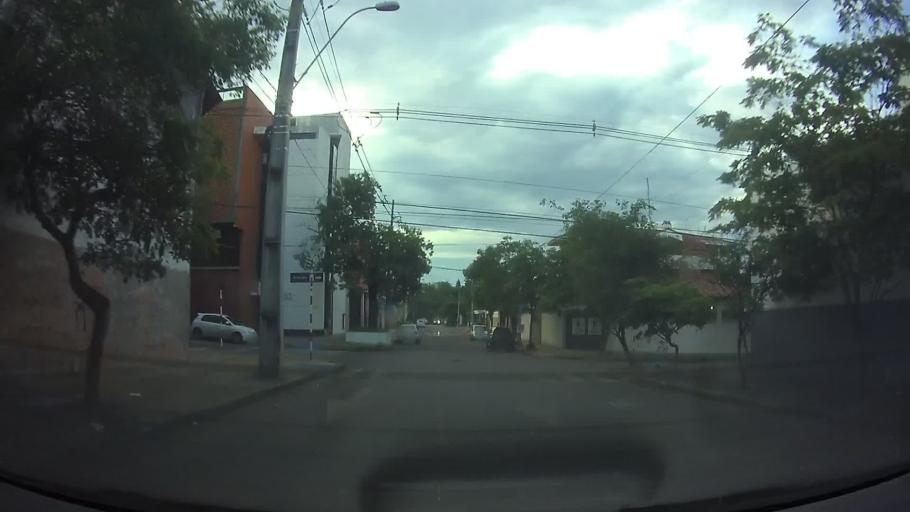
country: PY
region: Asuncion
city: Asuncion
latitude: -25.2849
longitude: -57.5734
